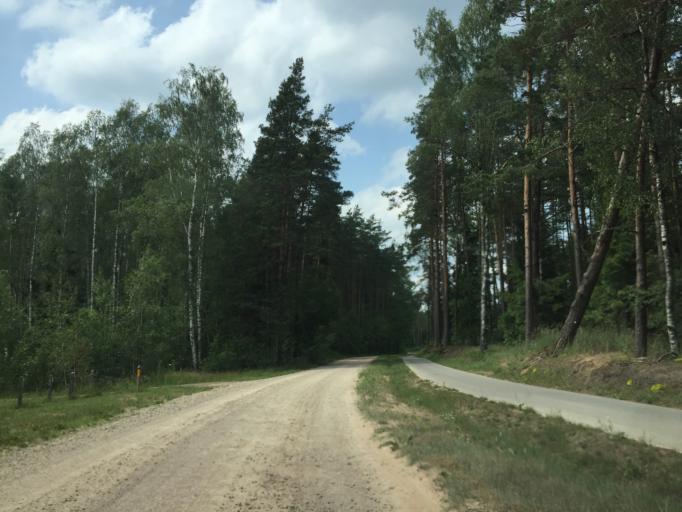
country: LV
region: Olaine
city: Olaine
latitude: 56.7789
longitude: 23.8895
